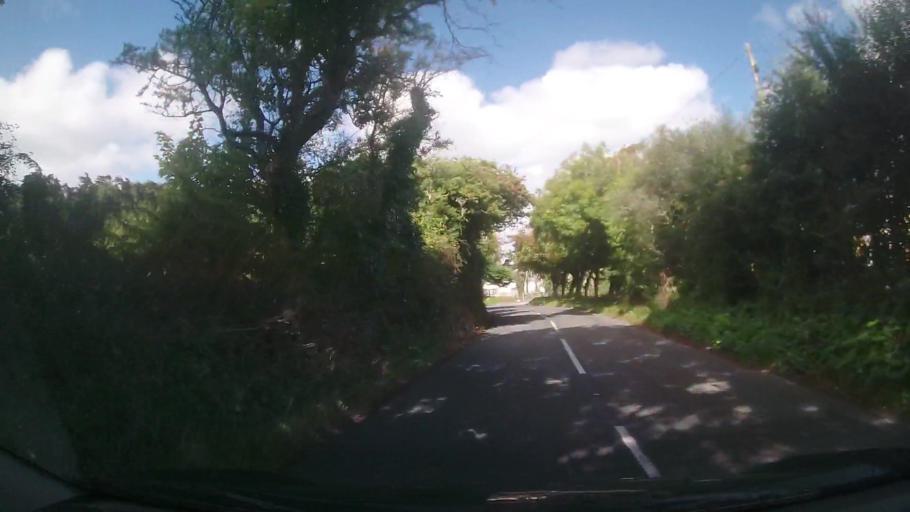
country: GB
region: Wales
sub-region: Pembrokeshire
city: Penally
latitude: 51.6560
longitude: -4.7395
